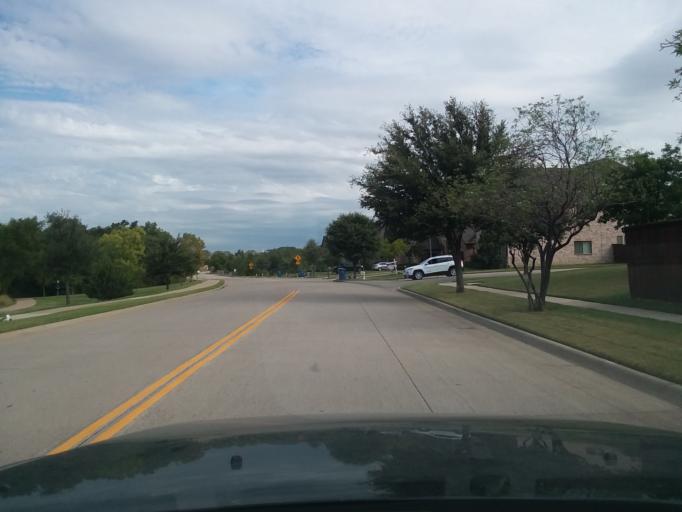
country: US
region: Texas
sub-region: Denton County
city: Copper Canyon
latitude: 33.1081
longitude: -97.1216
